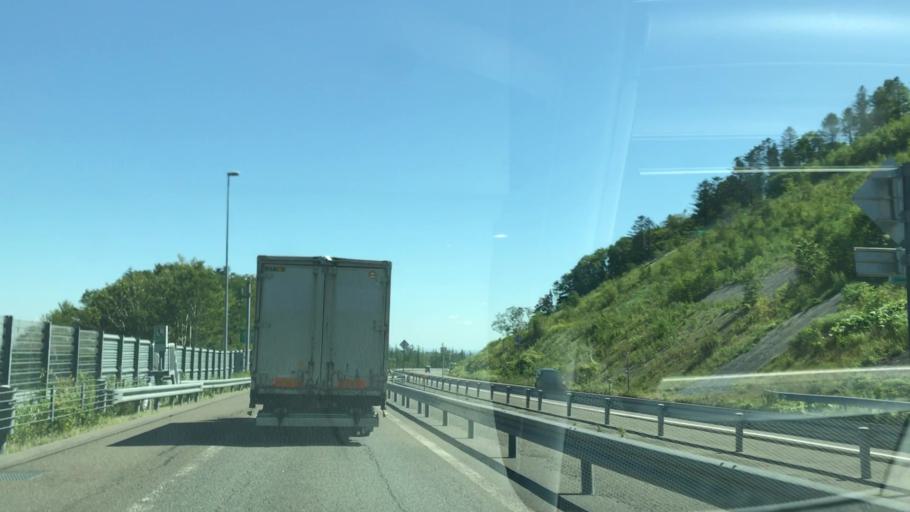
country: JP
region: Hokkaido
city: Otofuke
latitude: 43.0702
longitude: 142.7573
